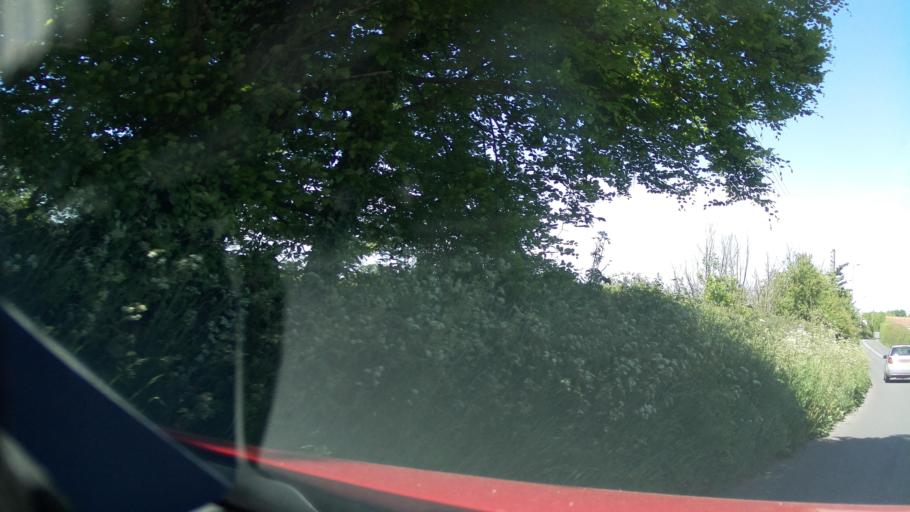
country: GB
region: England
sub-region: Devon
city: Starcross
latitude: 50.6565
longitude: -3.4207
